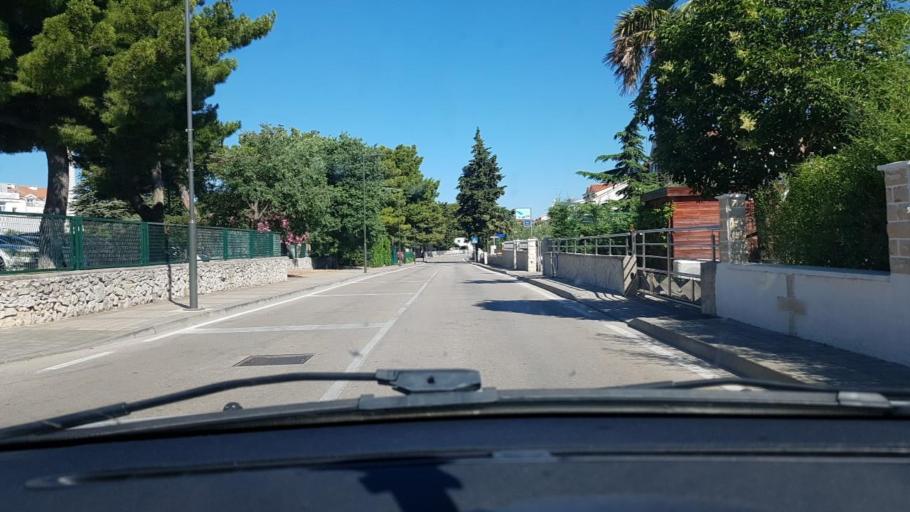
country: HR
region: Sibensko-Kniniska
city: Vodice
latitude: 43.7565
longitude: 15.7867
